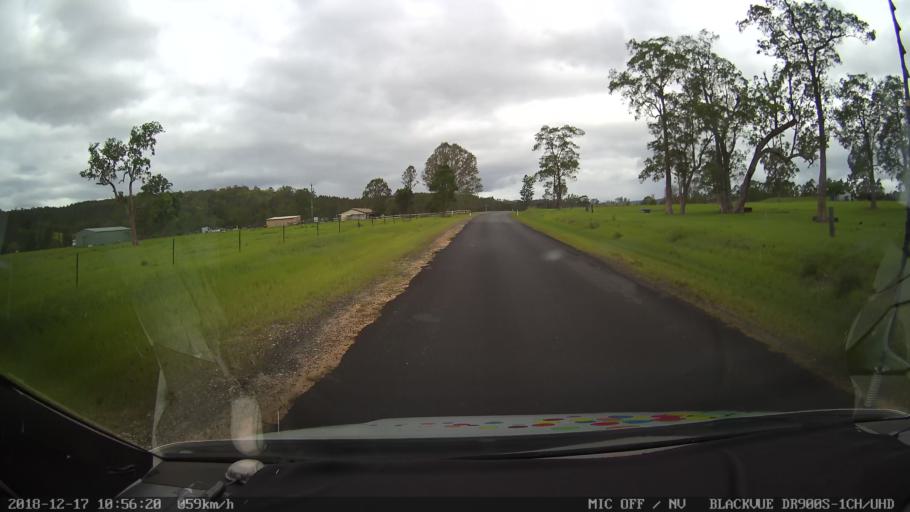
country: AU
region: New South Wales
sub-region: Richmond Valley
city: Casino
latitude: -28.8224
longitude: 152.5868
